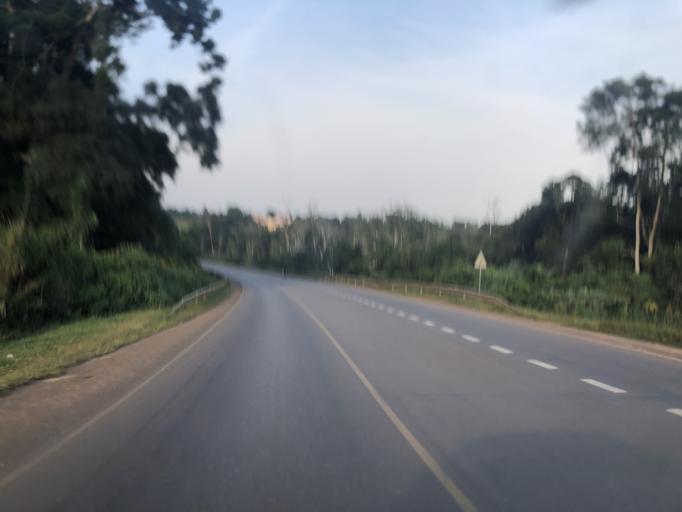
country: UG
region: Central Region
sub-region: Mpigi District
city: Mpigi
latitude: 0.2028
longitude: 32.3064
